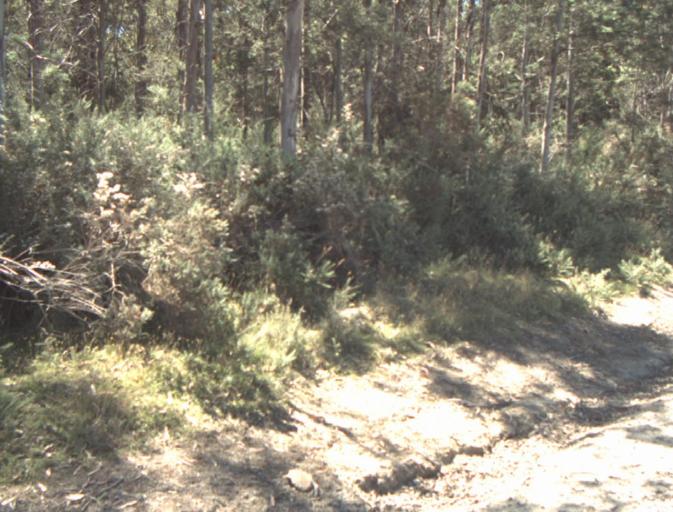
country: AU
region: Tasmania
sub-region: Dorset
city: Scottsdale
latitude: -41.3280
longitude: 147.4850
